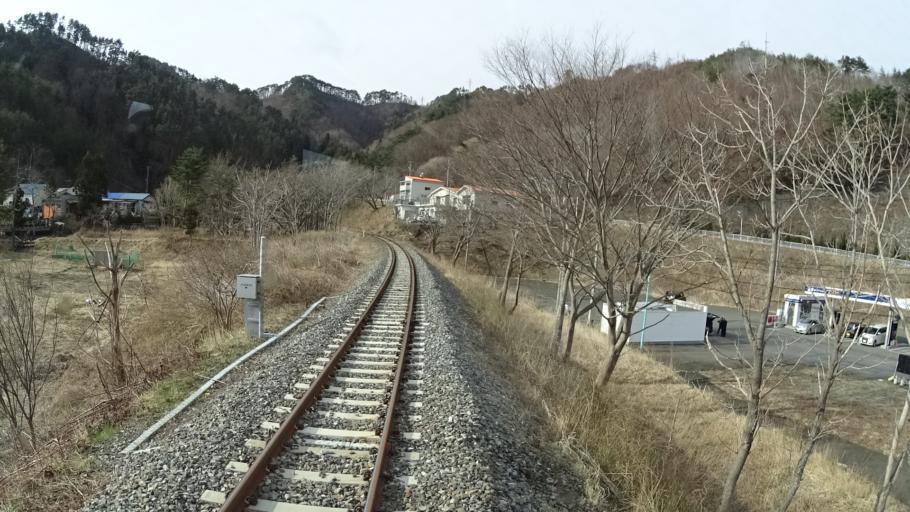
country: JP
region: Iwate
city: Otsuchi
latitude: 39.3535
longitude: 141.8942
